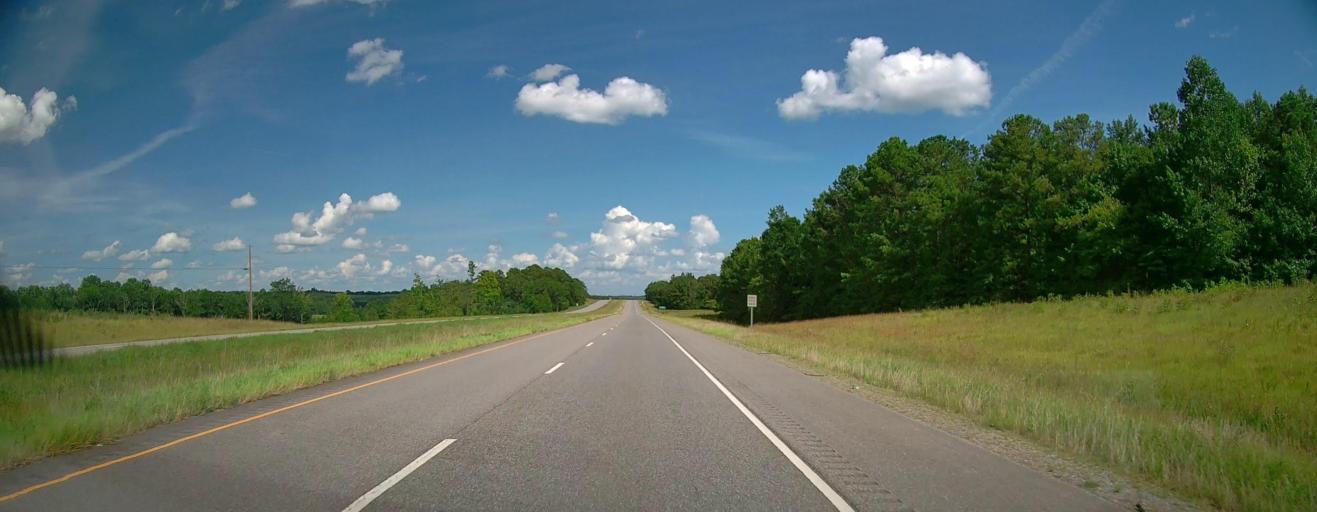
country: US
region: Alabama
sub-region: Pickens County
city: Reform
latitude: 33.3945
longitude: -88.0524
